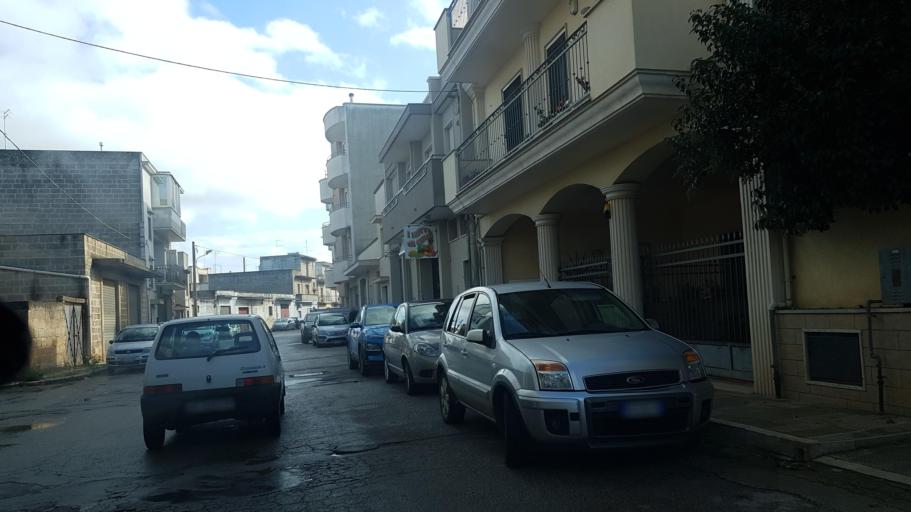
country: IT
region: Apulia
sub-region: Provincia di Brindisi
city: Carovigno
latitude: 40.7139
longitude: 17.6571
